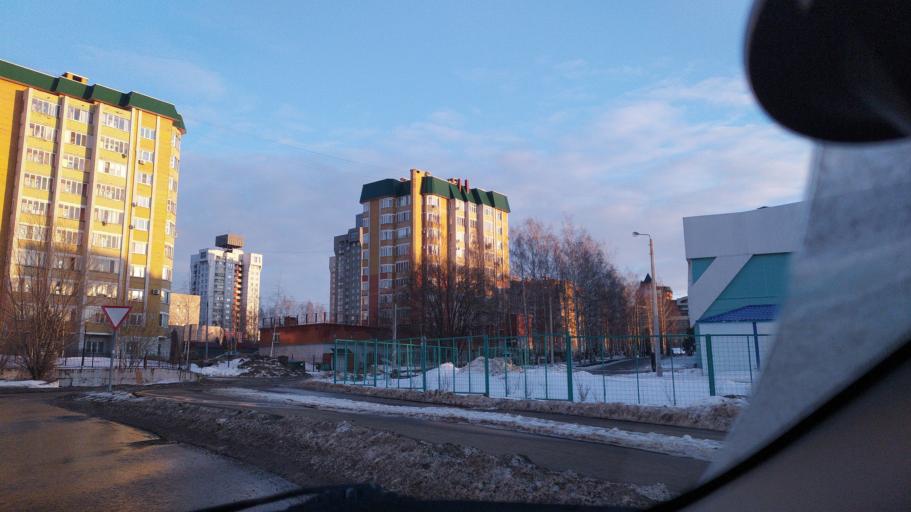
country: RU
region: Chuvashia
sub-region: Cheboksarskiy Rayon
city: Cheboksary
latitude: 56.1488
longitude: 47.2131
